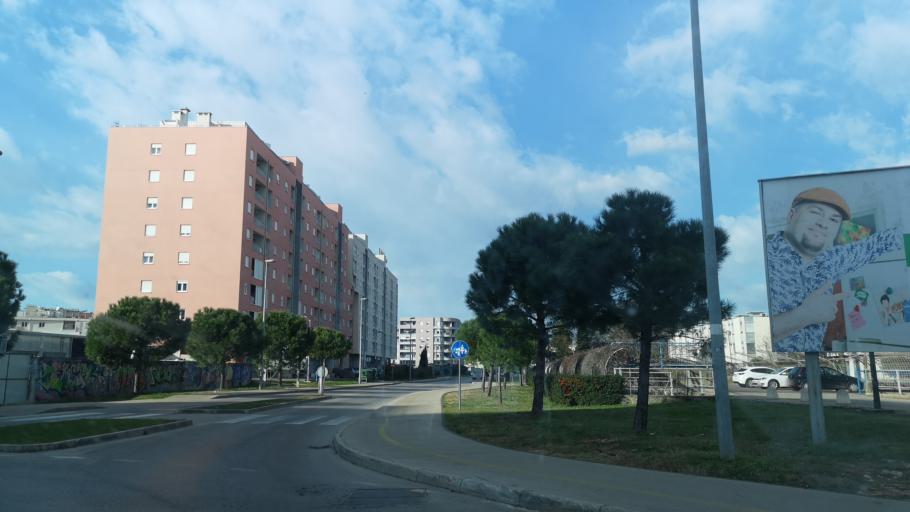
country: HR
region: Zadarska
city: Zadar
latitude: 44.1208
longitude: 15.2394
